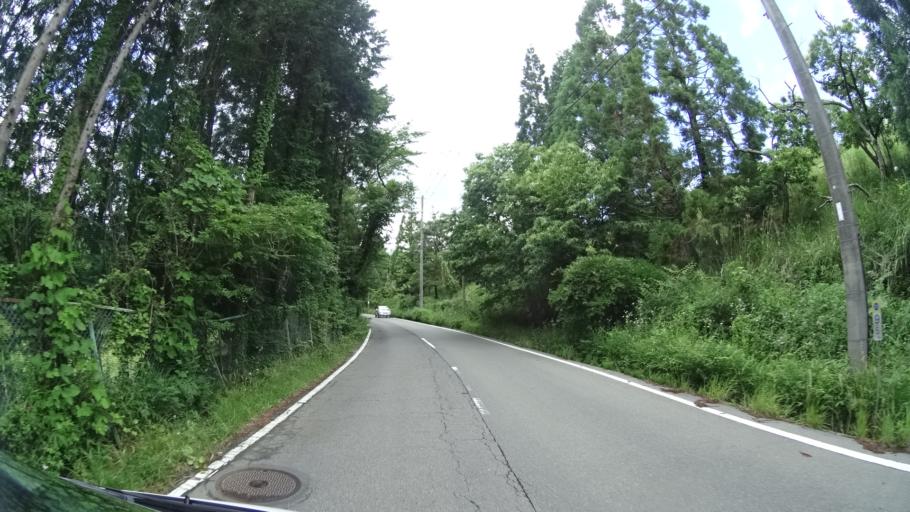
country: JP
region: Kyoto
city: Kameoka
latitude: 35.0102
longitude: 135.4591
